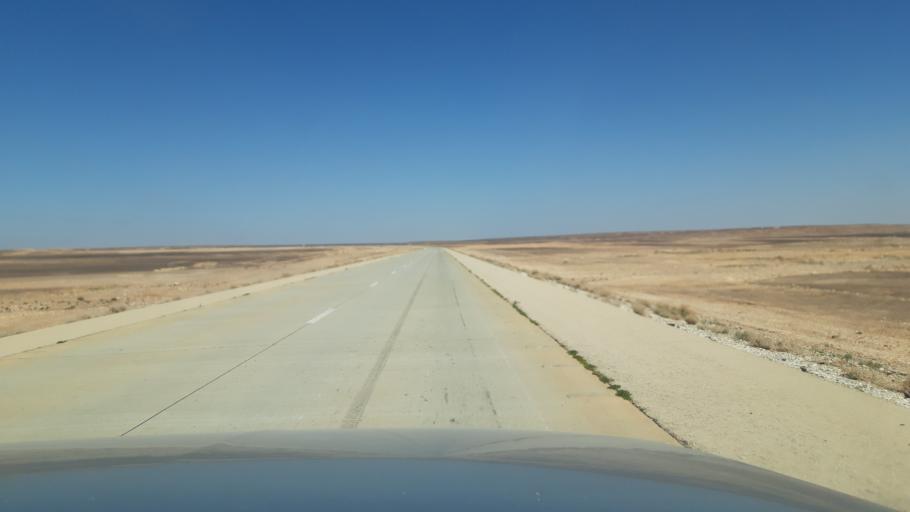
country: SA
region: Al Jawf
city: Al Qurayyat
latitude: 31.1005
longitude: 36.6400
